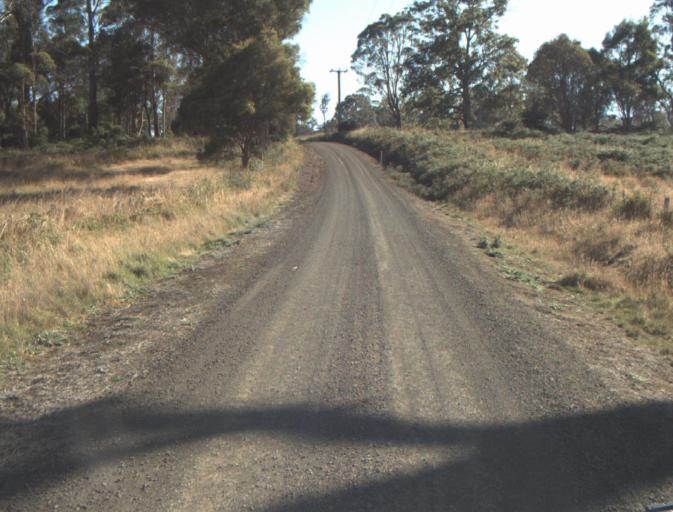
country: AU
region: Tasmania
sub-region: Launceston
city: Newstead
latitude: -41.4153
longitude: 147.2857
